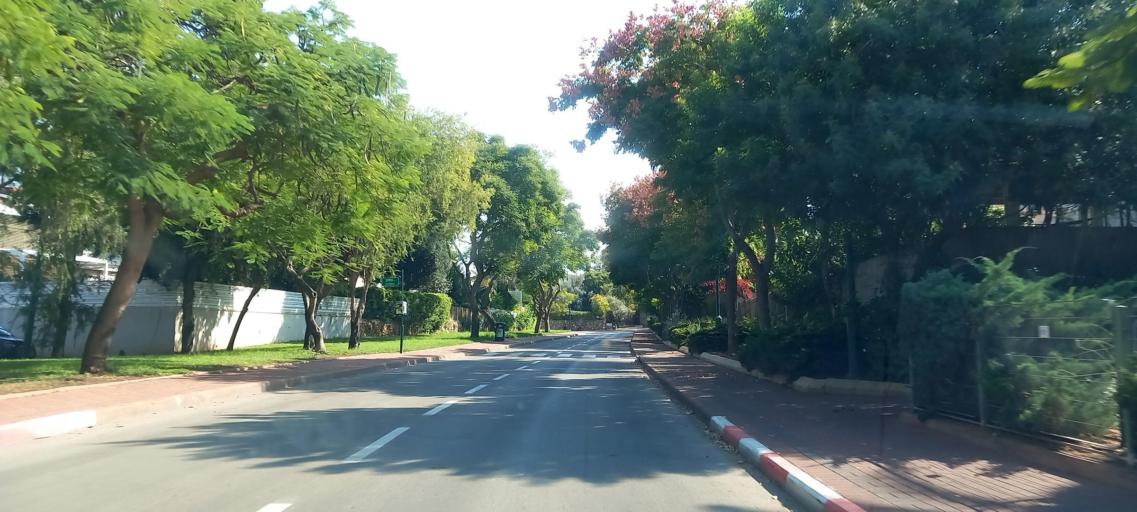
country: IL
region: Tel Aviv
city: Or Yehuda
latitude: 32.0436
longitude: 34.8350
